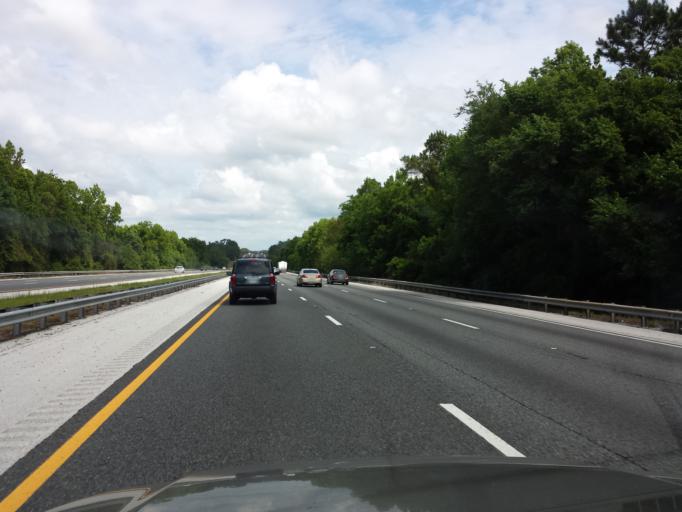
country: US
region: Florida
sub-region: Marion County
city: Citra
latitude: 29.4352
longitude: -82.2641
